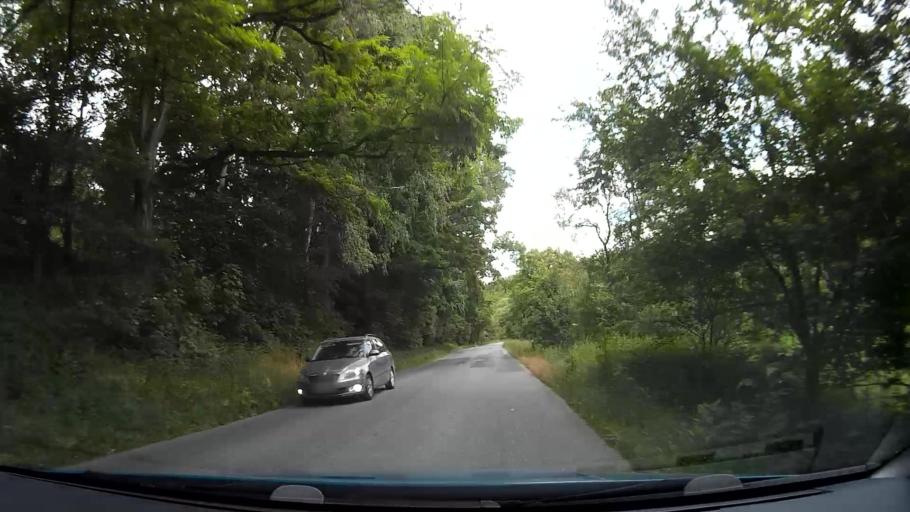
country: CZ
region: South Moravian
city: Ostopovice
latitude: 49.1432
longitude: 16.5313
